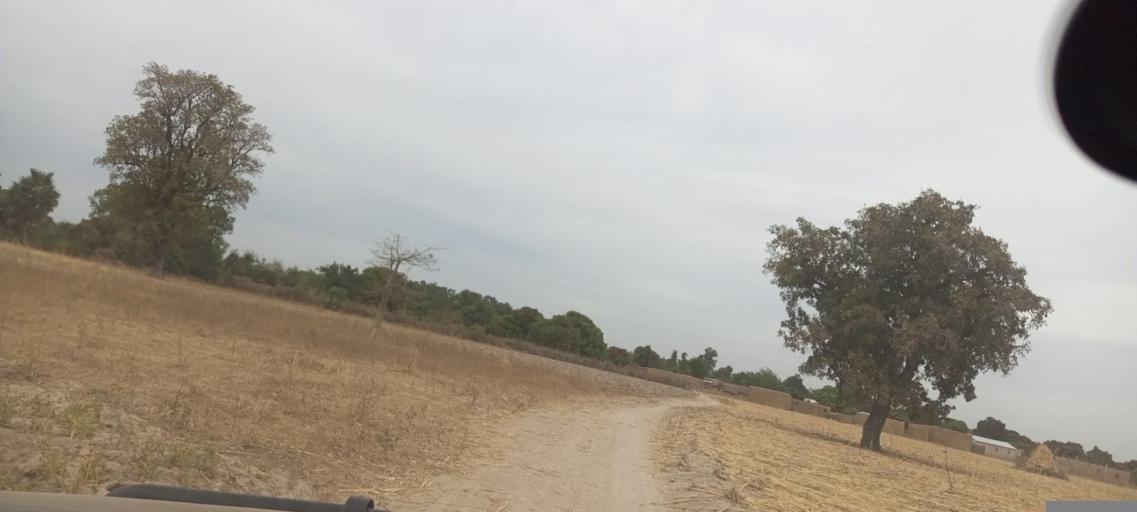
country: ML
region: Koulikoro
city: Kati
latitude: 12.7405
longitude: -8.3290
